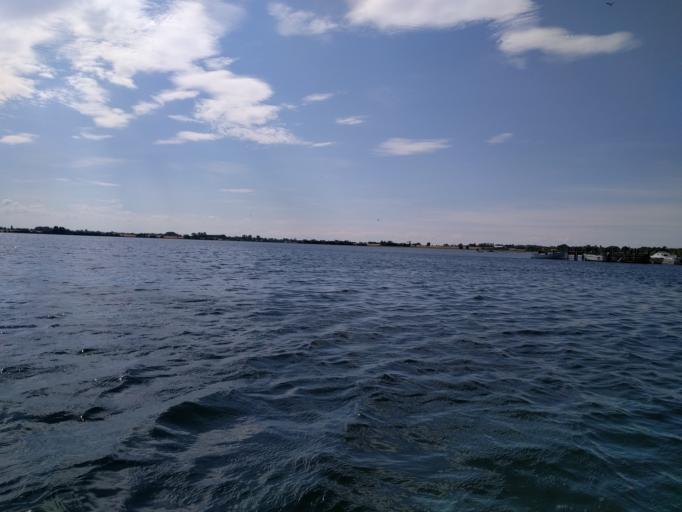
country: DK
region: South Denmark
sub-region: Kerteminde Kommune
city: Kerteminde
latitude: 55.4464
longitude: 10.6537
